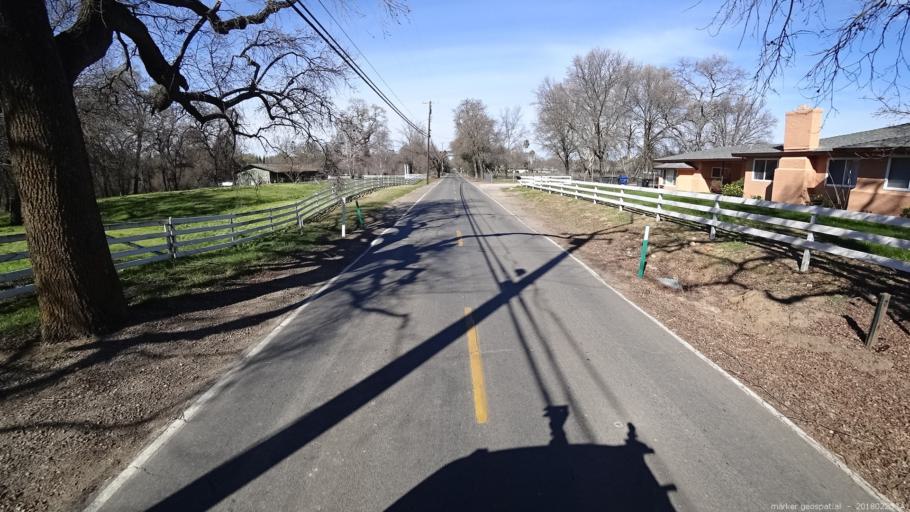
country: US
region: California
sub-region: Sacramento County
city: Orangevale
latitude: 38.7054
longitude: -121.2113
